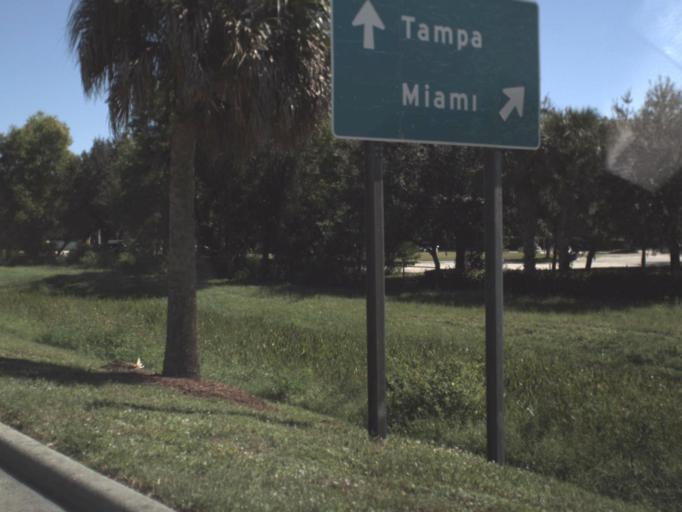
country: US
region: Florida
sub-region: Collier County
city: Vineyards
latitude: 26.2115
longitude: -81.7400
